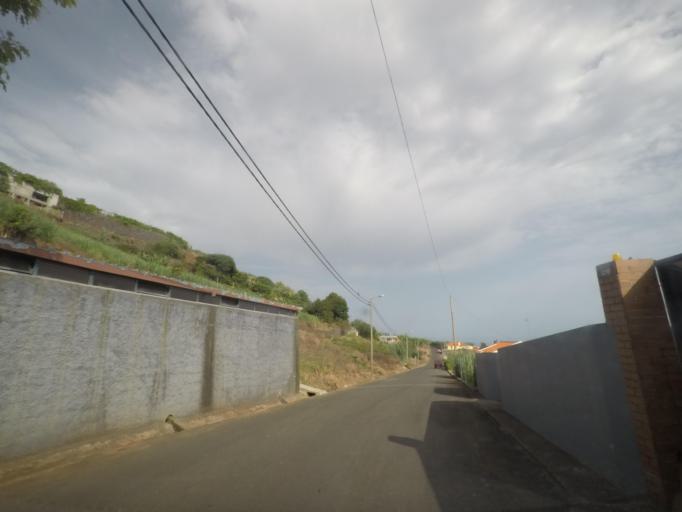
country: PT
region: Madeira
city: Ponta do Sol
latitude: 32.6951
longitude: -17.1195
